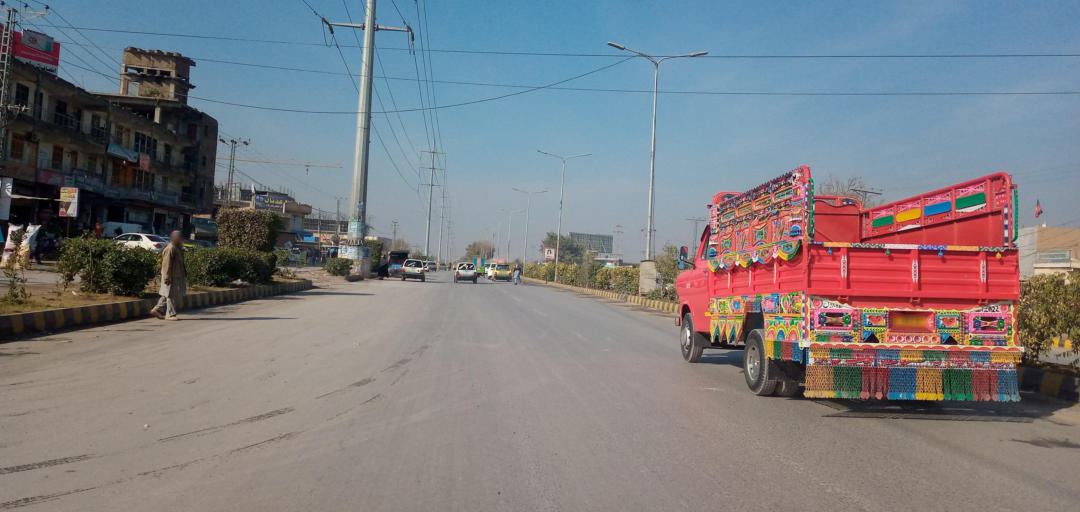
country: PK
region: Khyber Pakhtunkhwa
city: Peshawar
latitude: 33.9616
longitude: 71.5036
